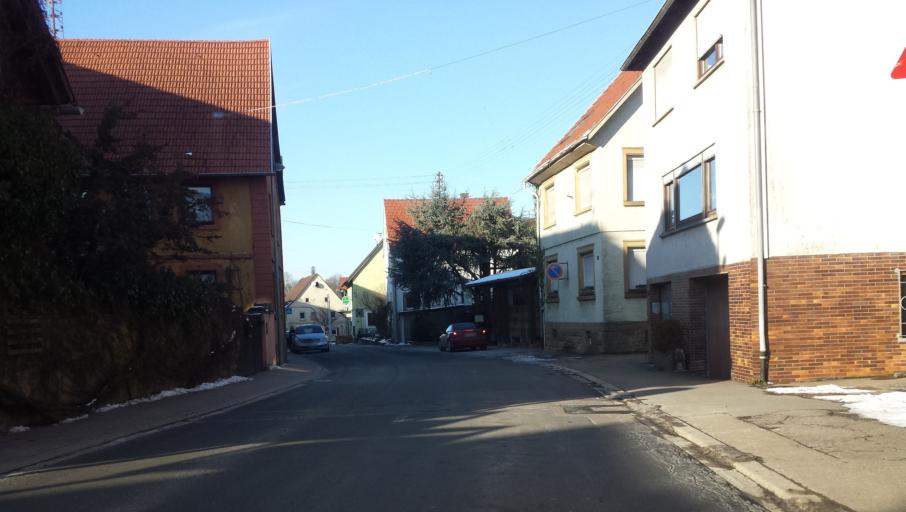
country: DE
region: Baden-Wuerttemberg
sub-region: Karlsruhe Region
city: Neidenstein
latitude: 49.2929
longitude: 8.8778
